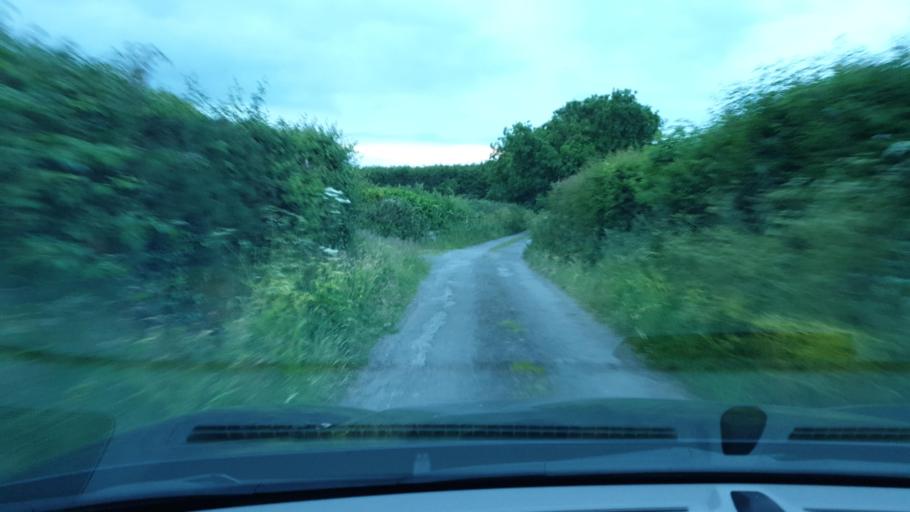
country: IE
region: Leinster
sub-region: An Mhi
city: Duleek
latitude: 53.5984
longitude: -6.3621
